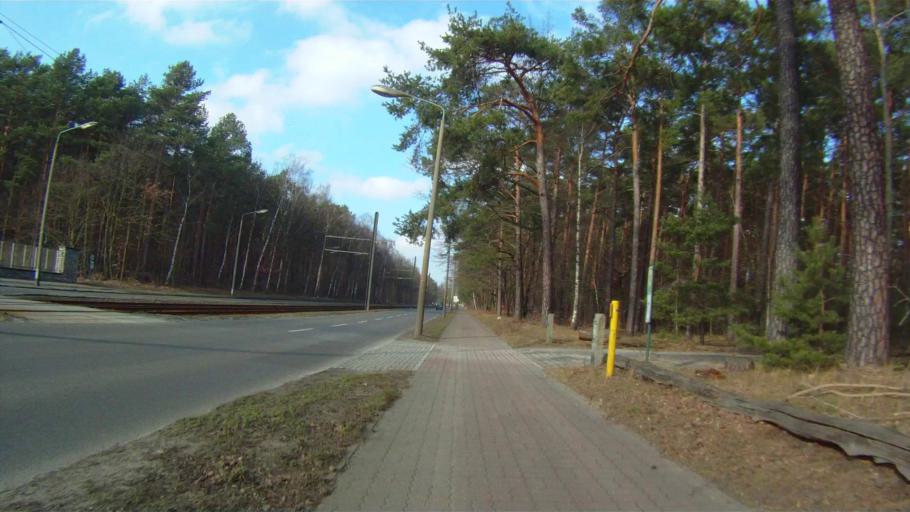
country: DE
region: Berlin
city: Schmockwitz
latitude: 52.3824
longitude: 13.6396
